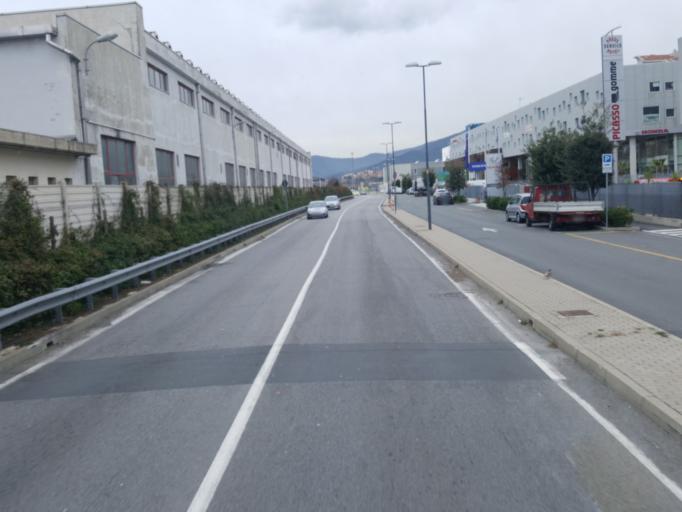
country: IT
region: Liguria
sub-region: Provincia di Savona
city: Savona
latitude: 44.3018
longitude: 8.4681
